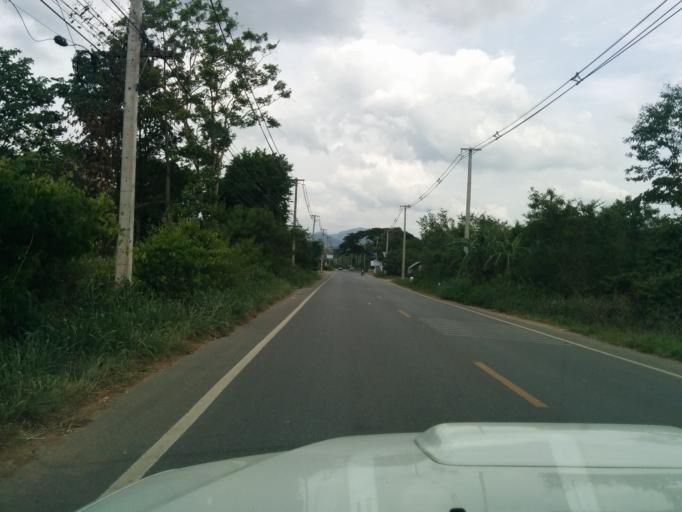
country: TH
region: Sara Buri
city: Muak Lek
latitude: 14.6186
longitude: 101.2124
